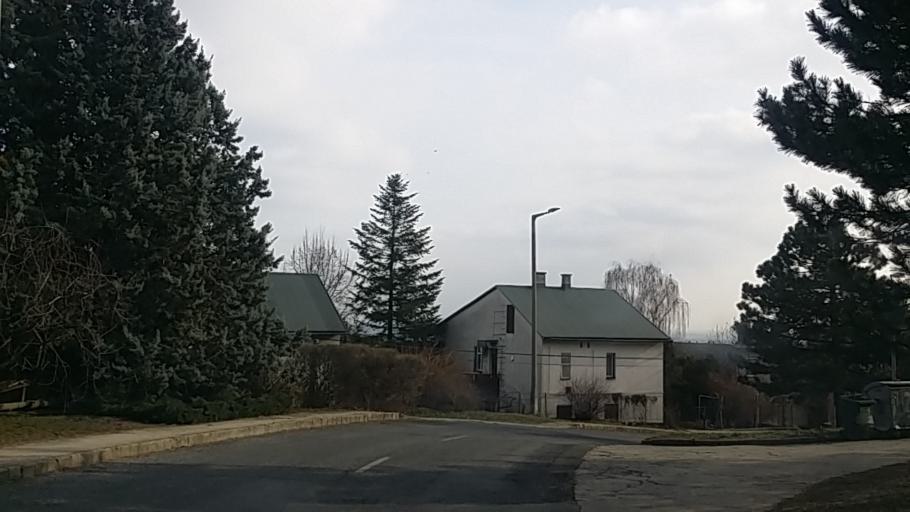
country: HU
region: Tolna
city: Szekszard
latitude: 46.3608
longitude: 18.6984
